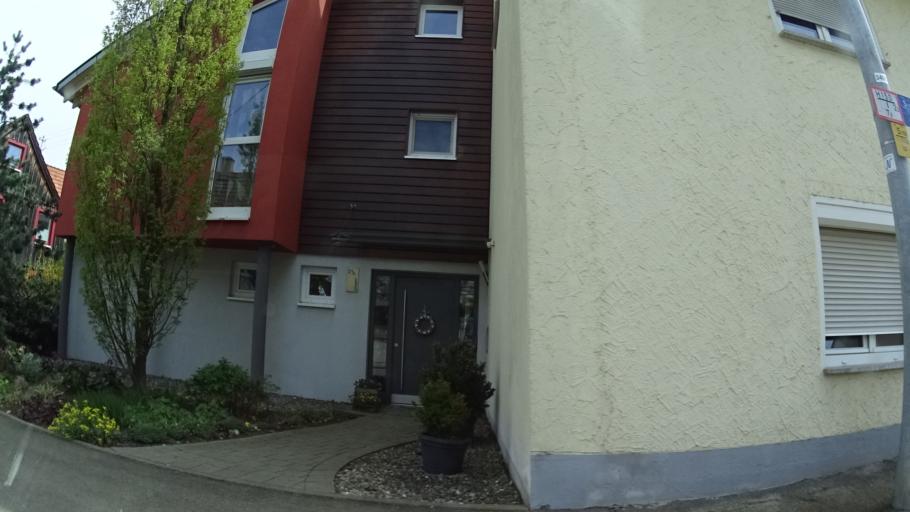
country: DE
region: Baden-Wuerttemberg
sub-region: Freiburg Region
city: Rottweil
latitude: 48.1444
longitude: 8.6293
